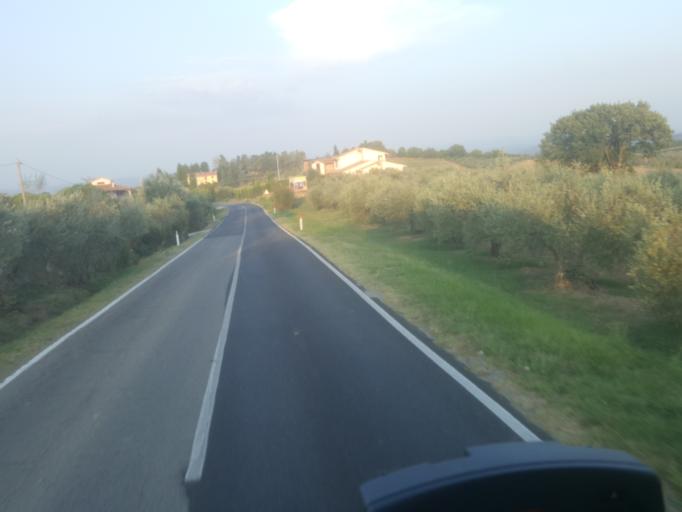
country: IT
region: Tuscany
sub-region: Province of Florence
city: Gambassi Terme
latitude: 43.5442
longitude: 10.9666
